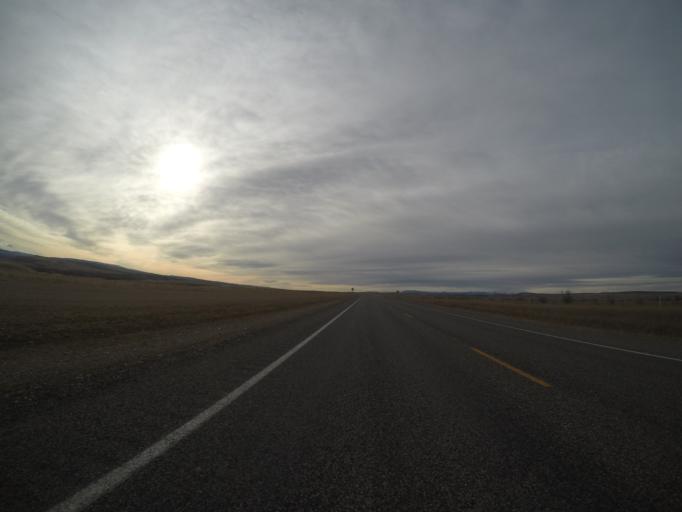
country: US
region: Montana
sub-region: Yellowstone County
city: Laurel
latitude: 45.5790
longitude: -108.8433
